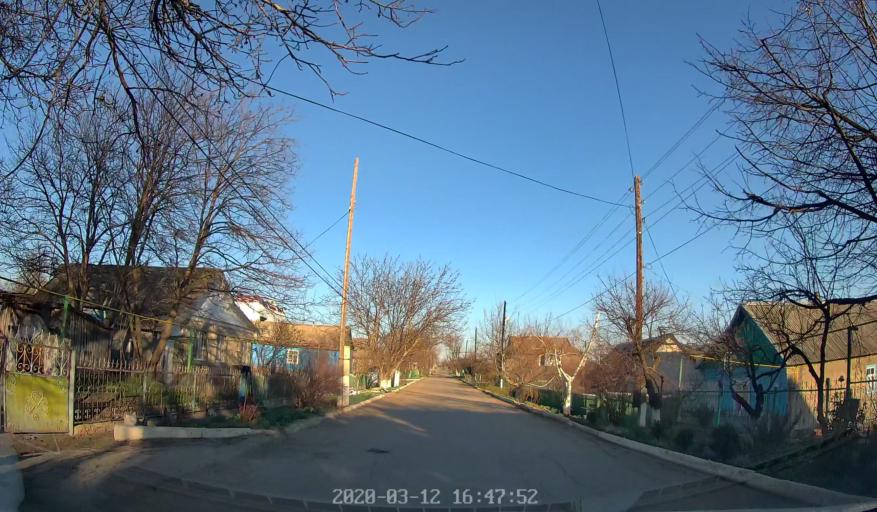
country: MD
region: Anenii Noi
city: Anenii Noi
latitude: 46.8137
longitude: 29.1890
